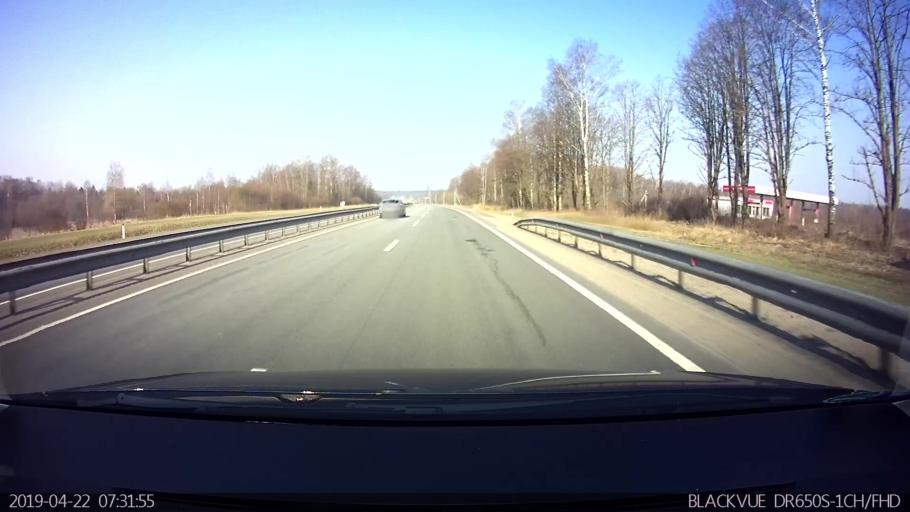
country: RU
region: Smolensk
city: Vyaz'ma
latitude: 55.1998
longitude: 33.9025
